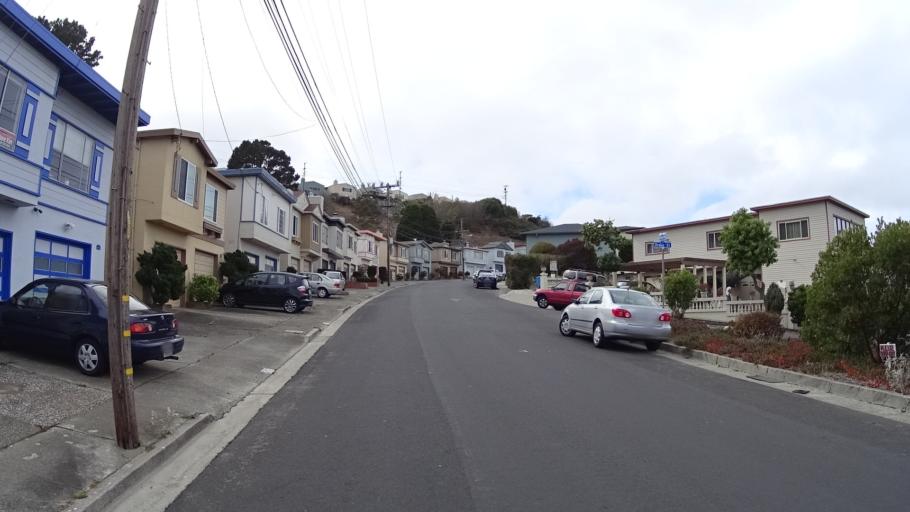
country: US
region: California
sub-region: San Mateo County
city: Daly City
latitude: 37.7081
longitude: -122.4347
